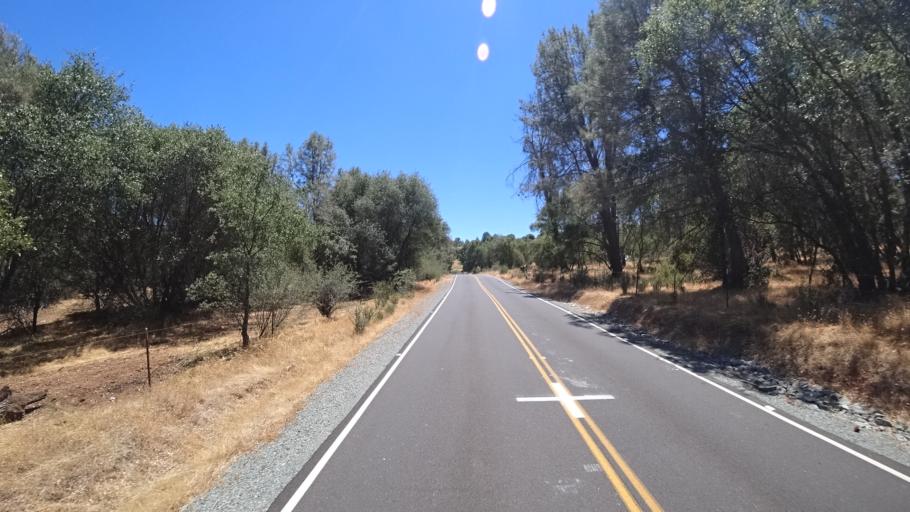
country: US
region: California
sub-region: Calaveras County
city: Copperopolis
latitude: 38.0489
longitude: -120.6499
